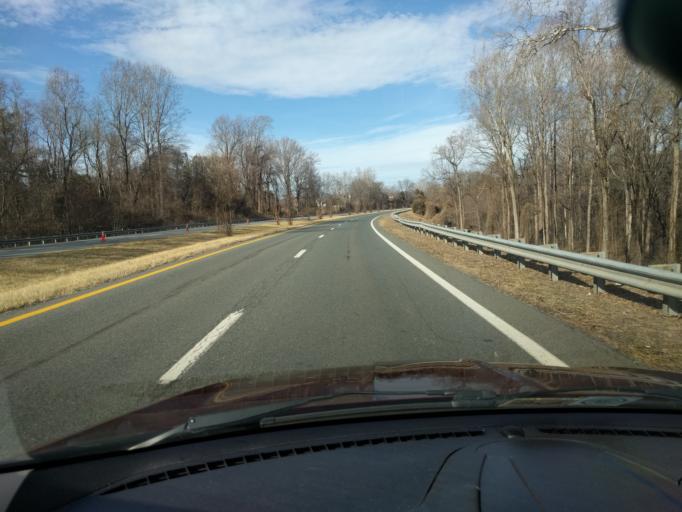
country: US
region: Virginia
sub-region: Amherst County
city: Madison Heights
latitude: 37.5166
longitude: -79.1170
